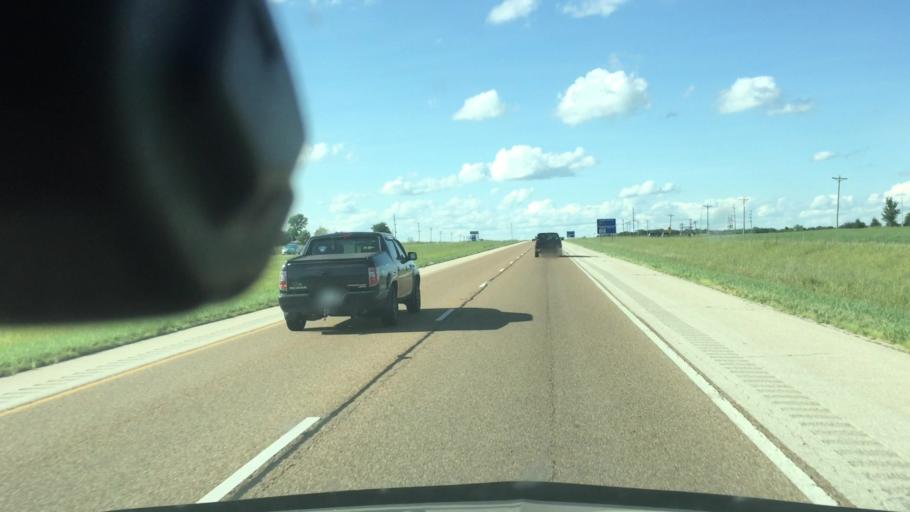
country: US
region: Illinois
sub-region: Montgomery County
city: Litchfield
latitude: 39.2518
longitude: -89.6412
